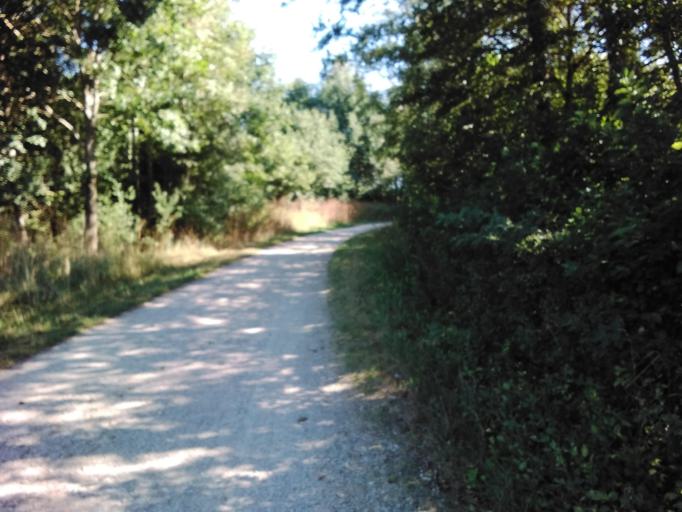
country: DE
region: Bavaria
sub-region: Regierungsbezirk Mittelfranken
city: Allersberg
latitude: 49.2343
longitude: 11.1996
